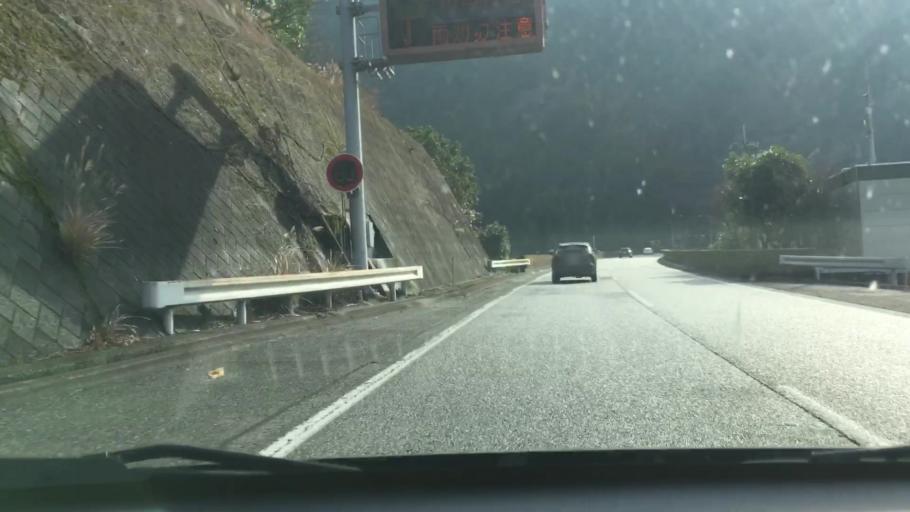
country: JP
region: Kumamoto
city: Yatsushiro
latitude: 32.4265
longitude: 130.7024
